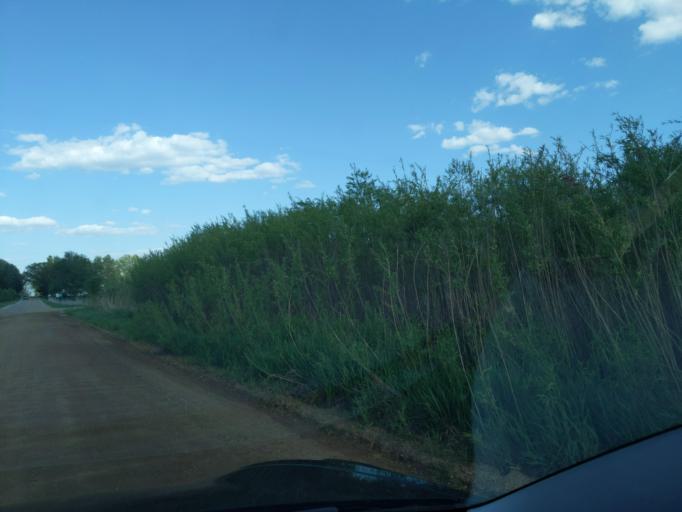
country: US
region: Michigan
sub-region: Eaton County
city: Potterville
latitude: 42.6828
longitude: -84.7214
